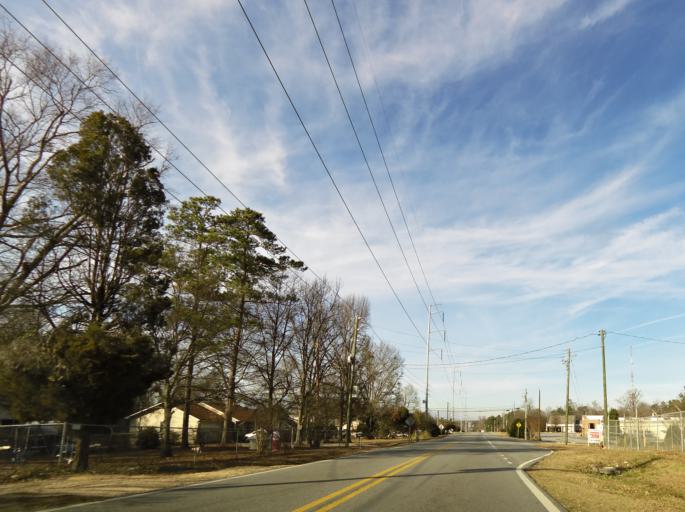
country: US
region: Georgia
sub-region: Bibb County
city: West Point
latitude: 32.8312
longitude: -83.7453
